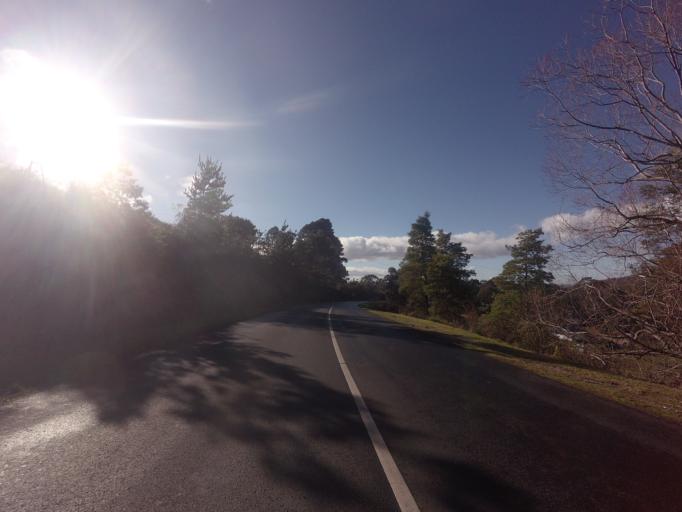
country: AU
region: Tasmania
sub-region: Glenorchy
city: Berriedale
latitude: -42.8255
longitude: 147.2004
